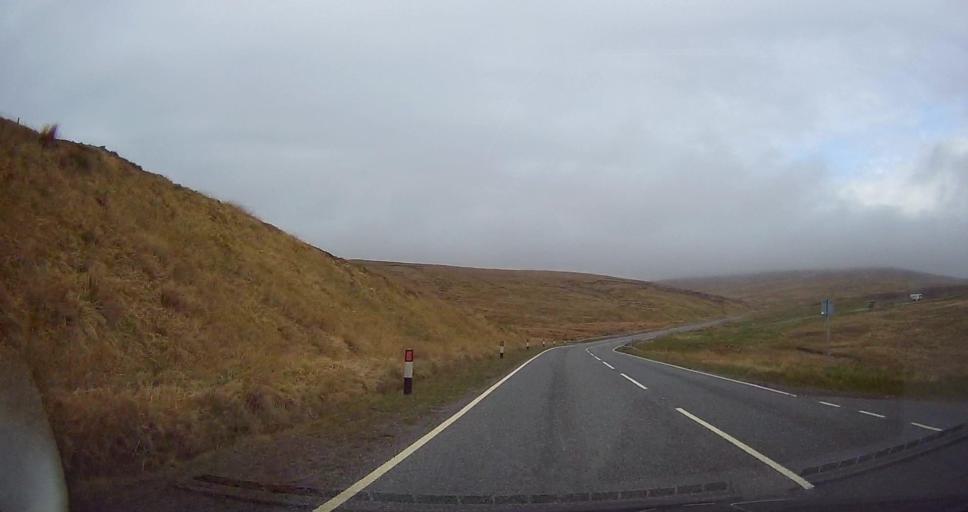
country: GB
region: Scotland
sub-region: Shetland Islands
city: Sandwick
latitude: 60.0018
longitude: -1.2803
